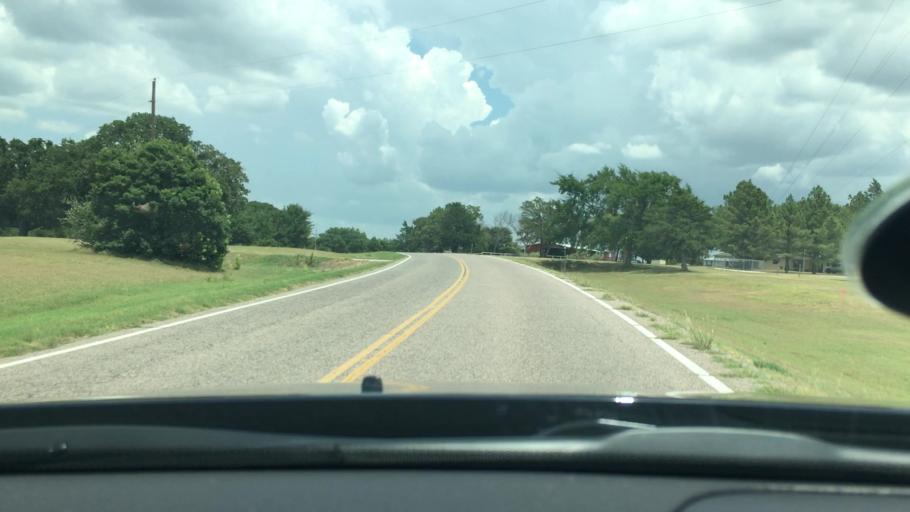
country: US
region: Oklahoma
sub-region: Marshall County
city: Oakland
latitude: 33.9846
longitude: -96.8857
